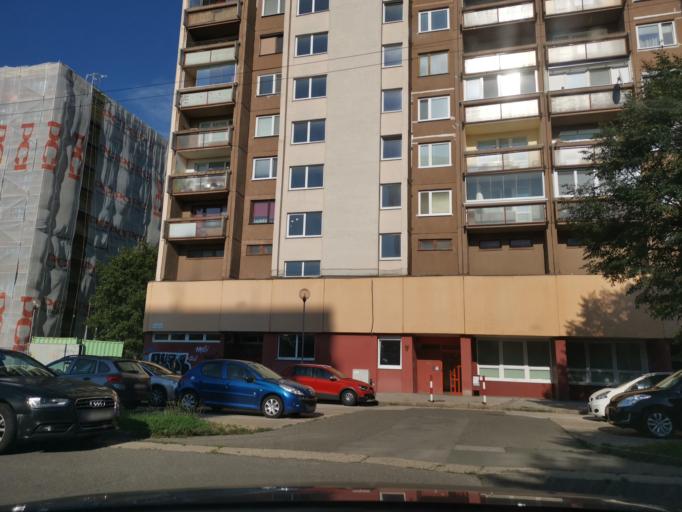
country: AT
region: Lower Austria
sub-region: Politischer Bezirk Bruck an der Leitha
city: Hainburg an der Donau
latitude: 48.2050
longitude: 16.9782
